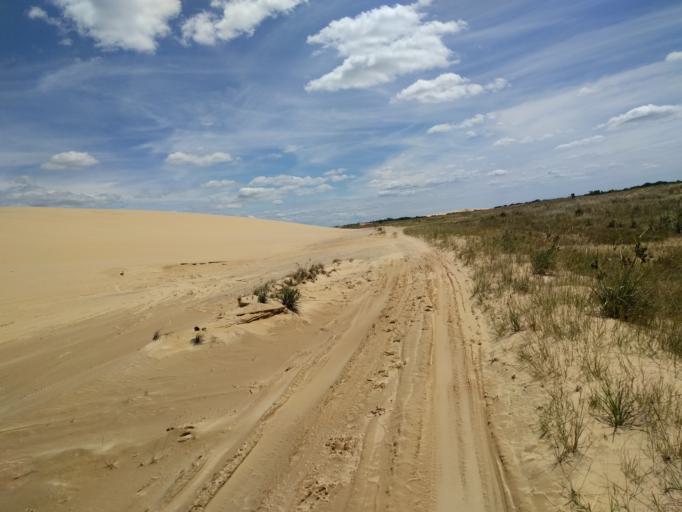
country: BO
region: Santa Cruz
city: Santa Cruz de la Sierra
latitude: -17.9403
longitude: -63.1571
